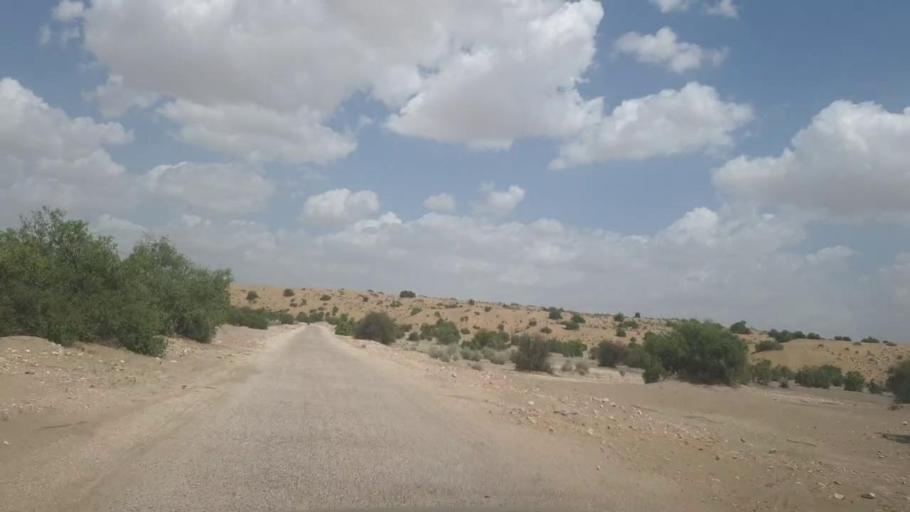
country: PK
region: Sindh
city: Kot Diji
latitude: 27.2527
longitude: 69.1585
